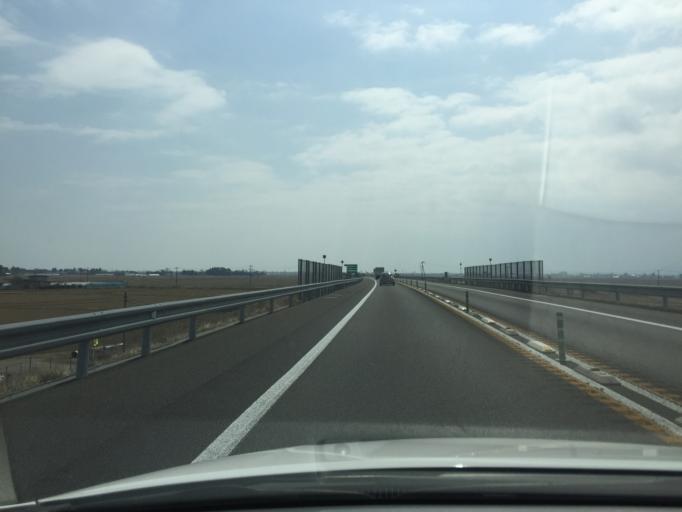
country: JP
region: Miyagi
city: Iwanuma
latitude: 38.0797
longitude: 140.8879
